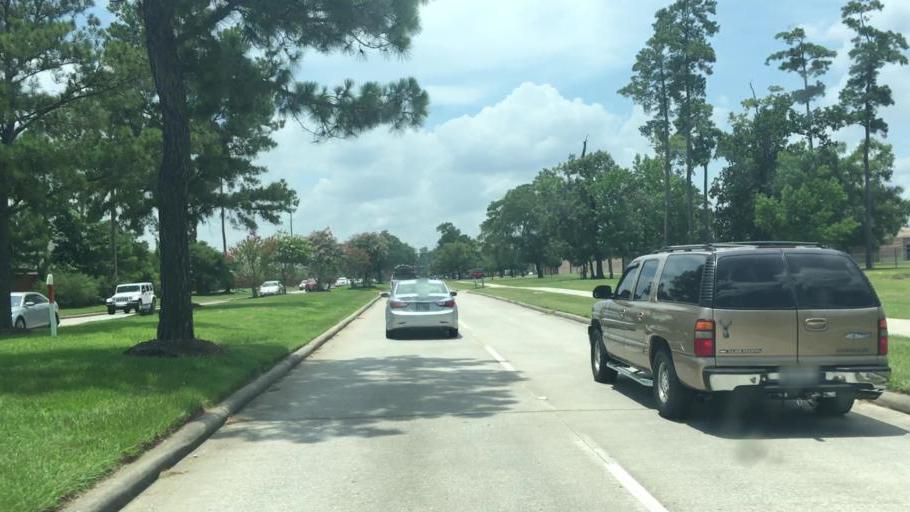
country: US
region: Texas
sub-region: Harris County
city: Atascocita
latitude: 29.9780
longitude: -95.2083
